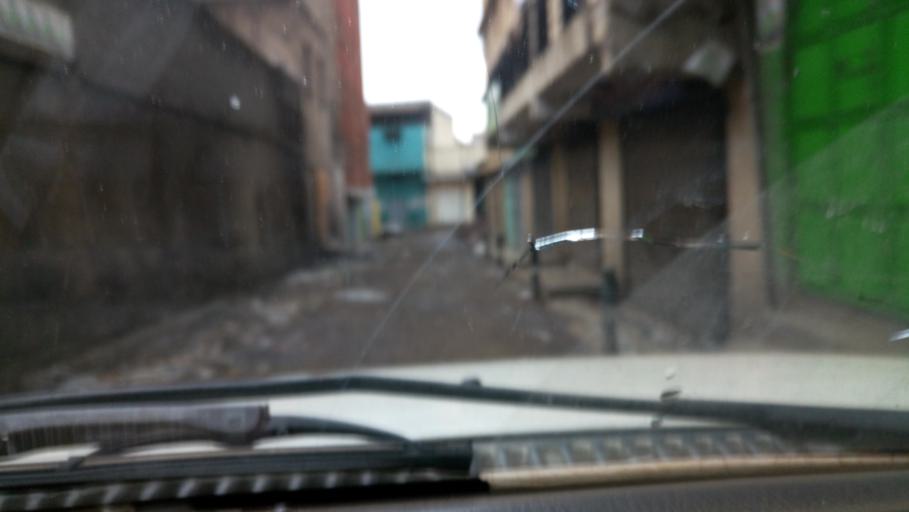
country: KE
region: Nairobi Area
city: Nairobi
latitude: -1.2824
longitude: 36.8305
